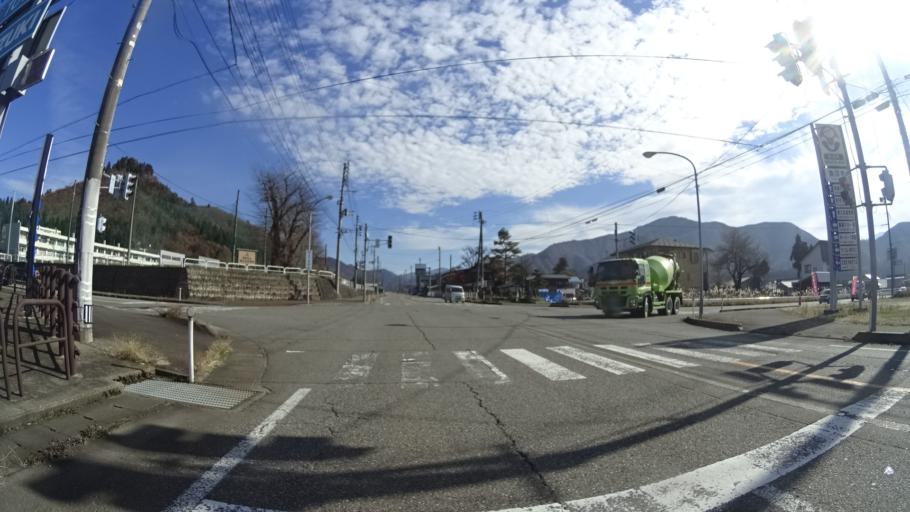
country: JP
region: Niigata
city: Muikamachi
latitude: 37.2288
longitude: 138.9843
